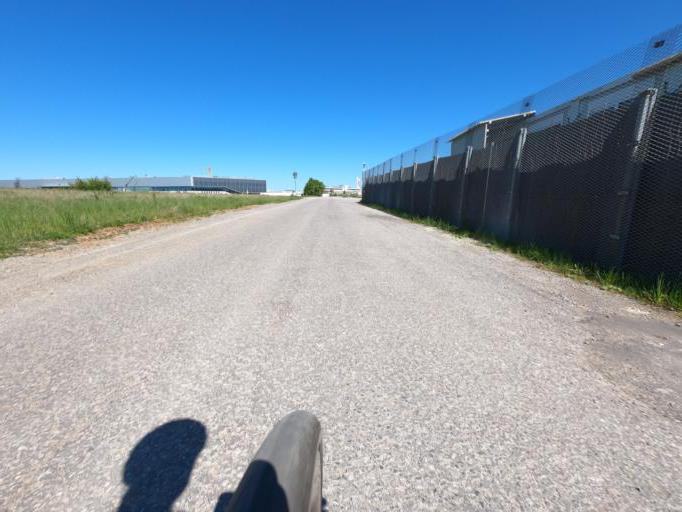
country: DE
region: Baden-Wuerttemberg
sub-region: Regierungsbezirk Stuttgart
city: Boeblingen
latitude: 48.6934
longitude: 8.9749
